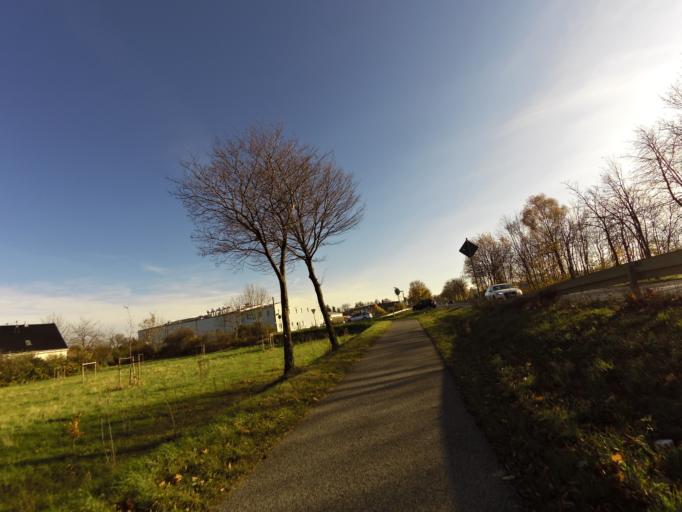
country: DE
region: North Rhine-Westphalia
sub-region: Regierungsbezirk Koln
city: Euskirchen
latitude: 50.6480
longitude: 6.8179
